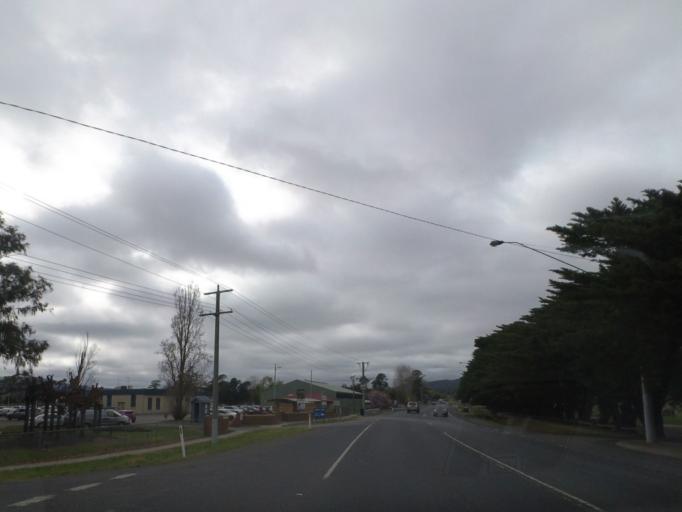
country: AU
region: Victoria
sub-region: Whittlesea
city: Whittlesea
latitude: -37.5106
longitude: 145.1250
